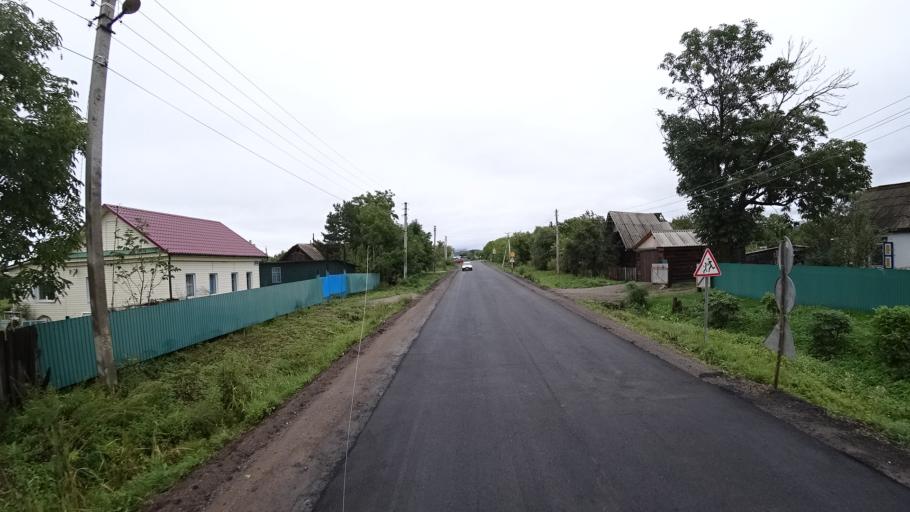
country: RU
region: Primorskiy
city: Monastyrishche
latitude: 44.1932
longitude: 132.4926
